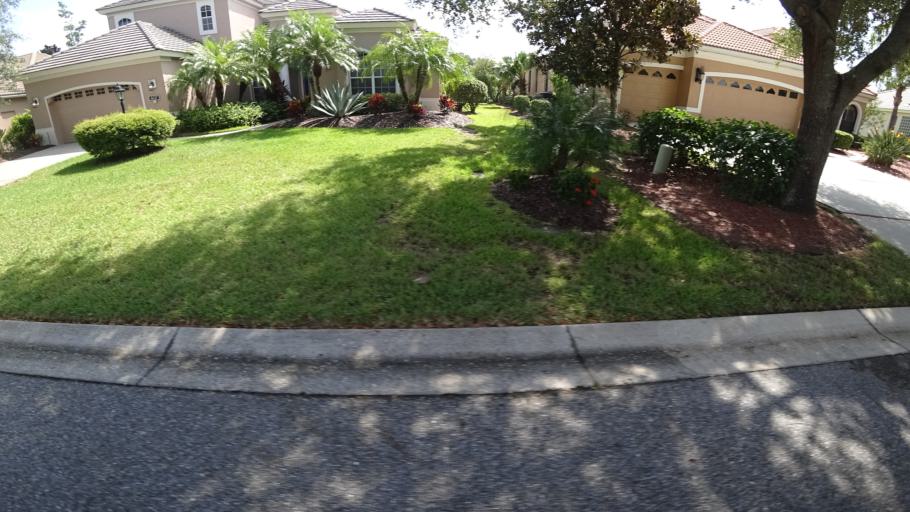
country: US
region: Florida
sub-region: Sarasota County
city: The Meadows
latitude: 27.4178
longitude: -82.4204
